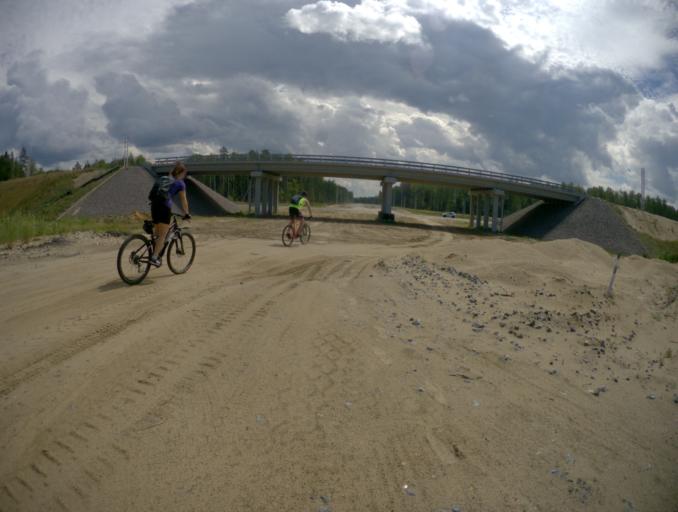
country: RU
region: Vladimir
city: Golovino
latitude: 56.0158
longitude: 40.5757
